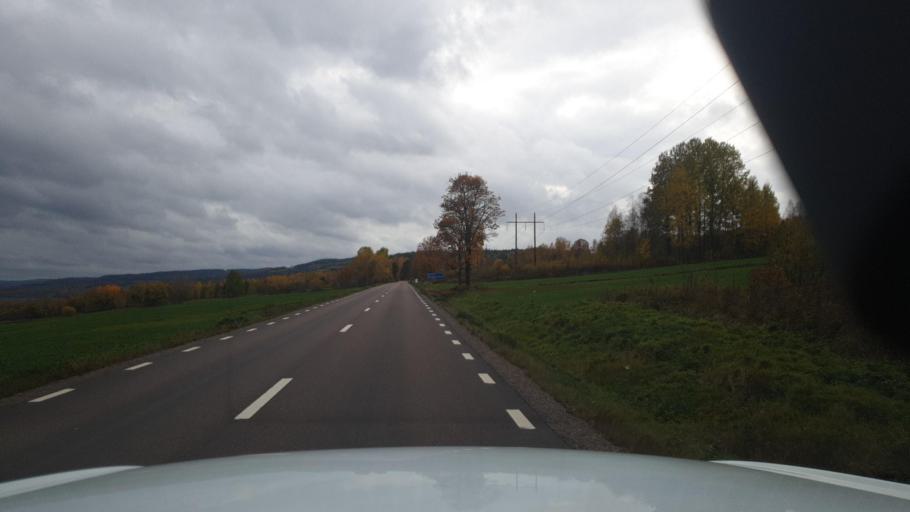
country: SE
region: Vaermland
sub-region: Torsby Kommun
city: Torsby
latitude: 59.9318
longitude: 12.8992
